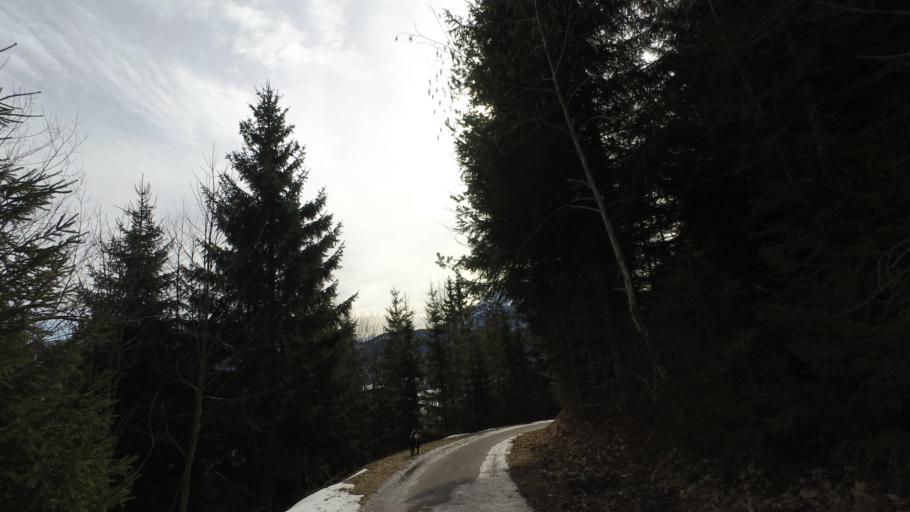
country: DE
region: Bavaria
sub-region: Upper Bavaria
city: Reit im Winkl
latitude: 47.6831
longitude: 12.4478
